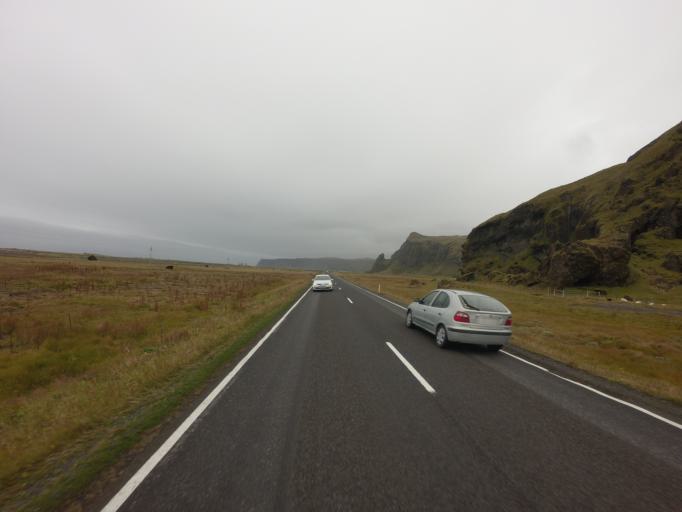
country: IS
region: South
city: Vestmannaeyjar
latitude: 63.4203
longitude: -18.9336
